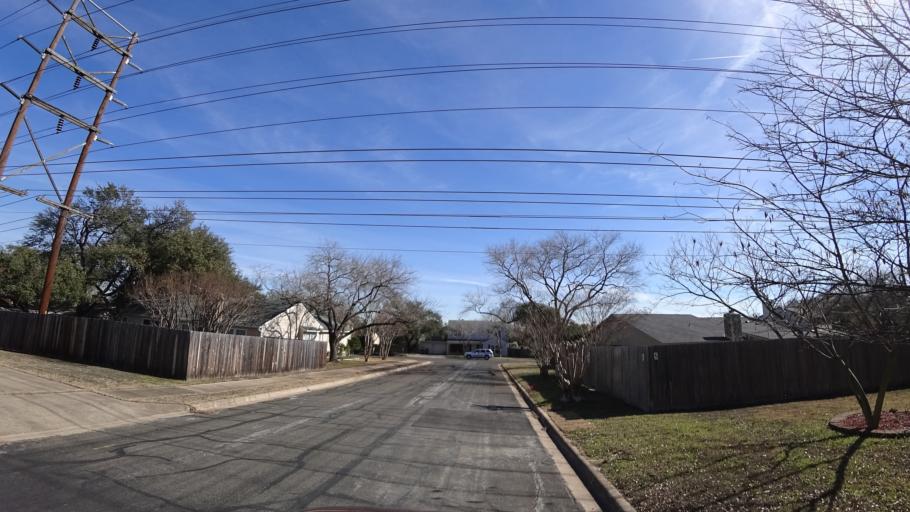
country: US
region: Texas
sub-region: Travis County
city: Wells Branch
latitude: 30.3896
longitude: -97.6890
